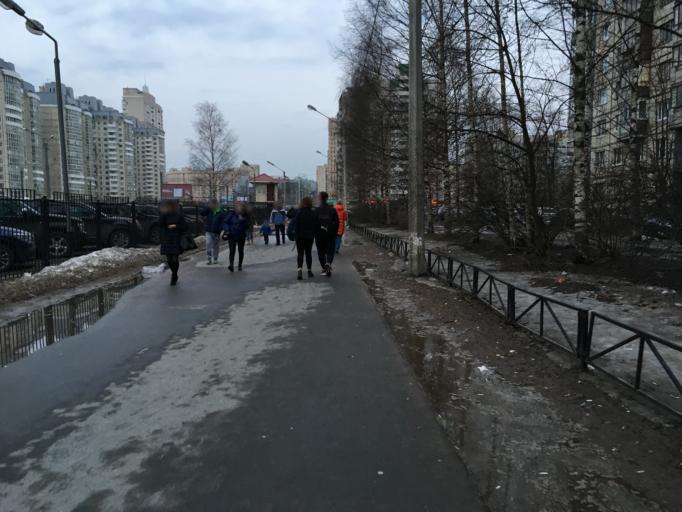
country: RU
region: St.-Petersburg
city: Komendantsky aerodrom
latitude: 60.0119
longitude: 30.2535
